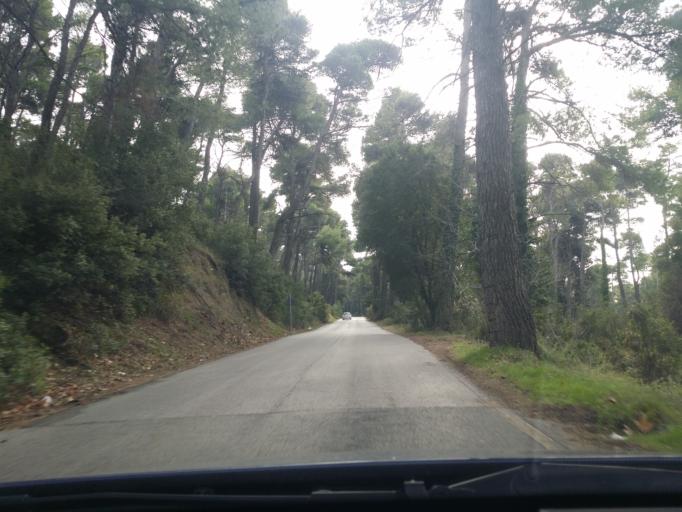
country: GR
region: Attica
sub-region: Nomarchia Anatolikis Attikis
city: Varybobi
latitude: 38.1548
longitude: 23.7918
